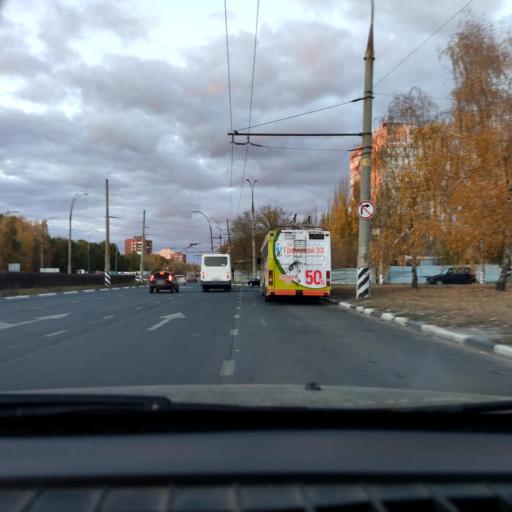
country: RU
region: Samara
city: Tol'yatti
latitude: 53.5060
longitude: 49.2920
